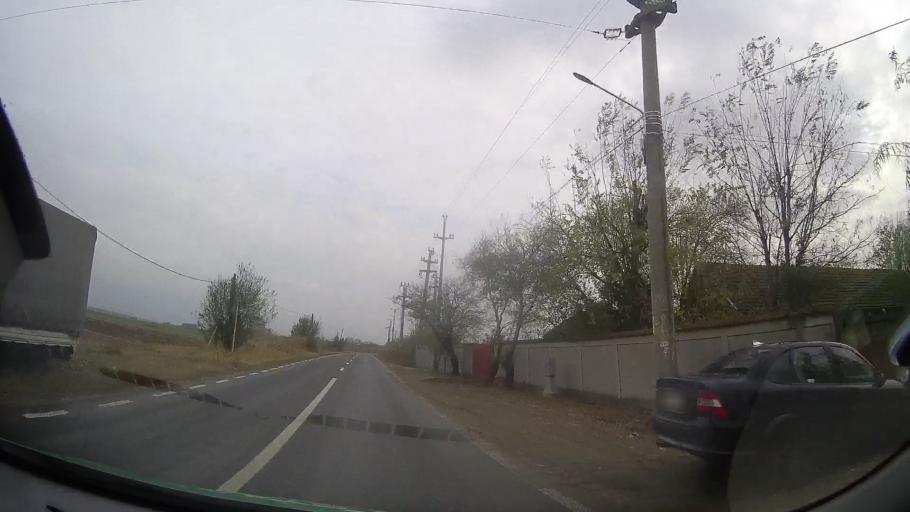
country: RO
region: Ilfov
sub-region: Comuna Gruiu
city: Lipia
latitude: 44.7198
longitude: 26.2703
